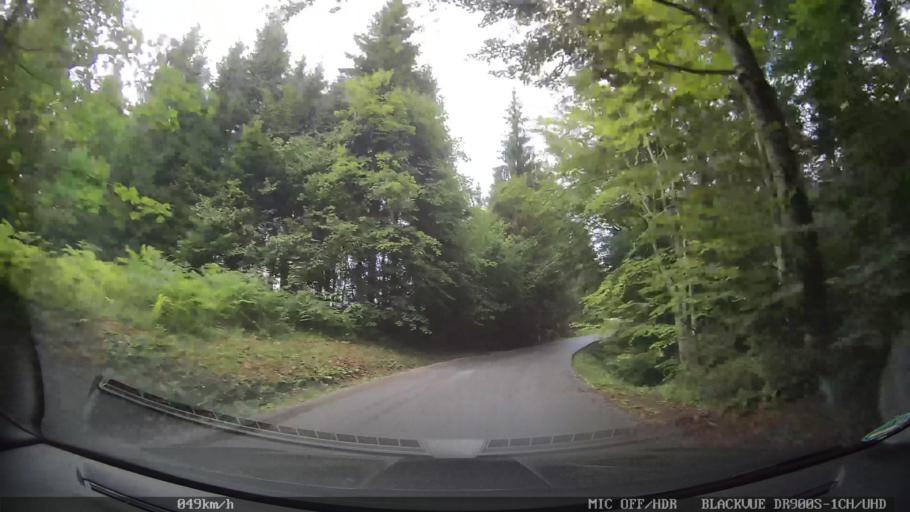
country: HR
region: Licko-Senjska
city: Jezerce
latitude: 44.9388
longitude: 15.5444
